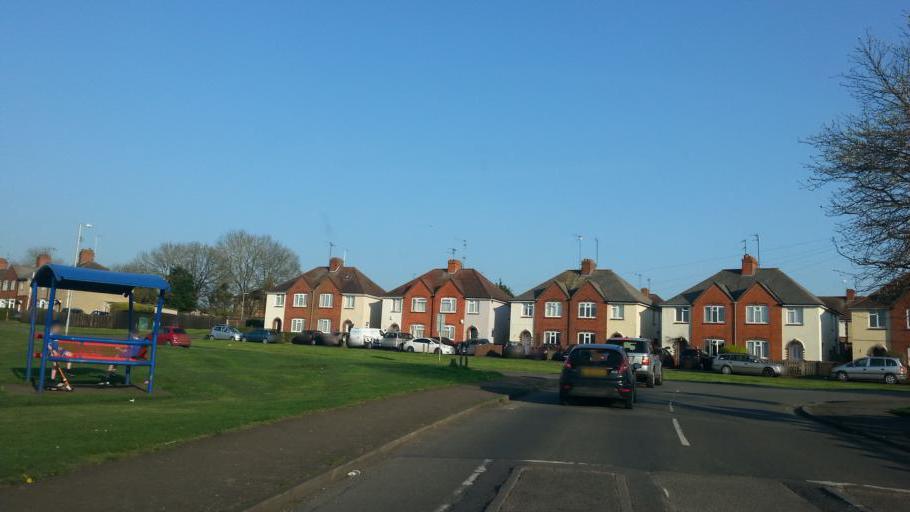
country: GB
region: England
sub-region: Northamptonshire
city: Rushden
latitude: 52.2906
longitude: -0.6173
